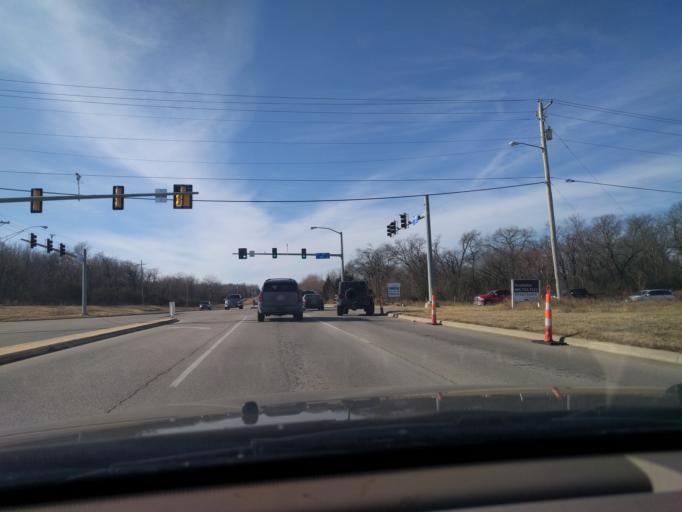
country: US
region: Oklahoma
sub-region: Tulsa County
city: Broken Arrow
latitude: 36.0609
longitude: -95.7434
